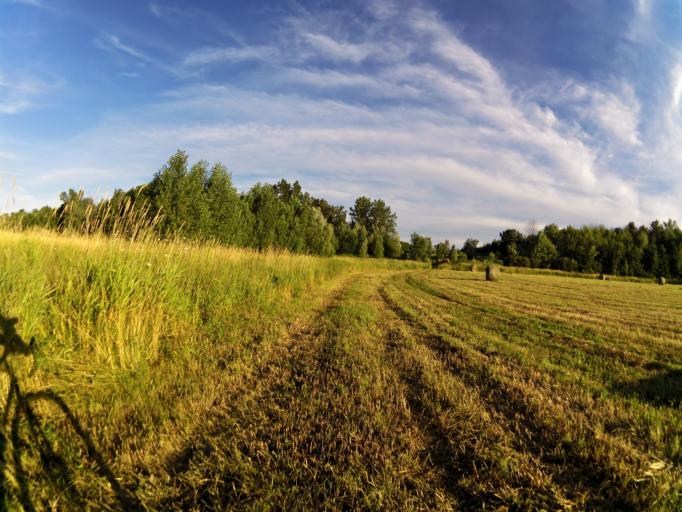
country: CA
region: Ontario
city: Ottawa
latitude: 45.4089
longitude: -75.5870
